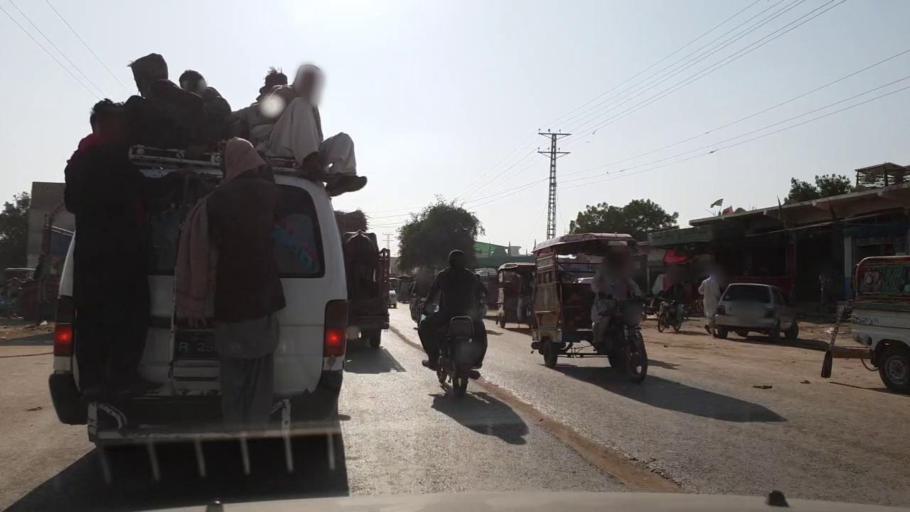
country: PK
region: Sindh
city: Tando Muhammad Khan
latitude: 25.1179
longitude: 68.5363
